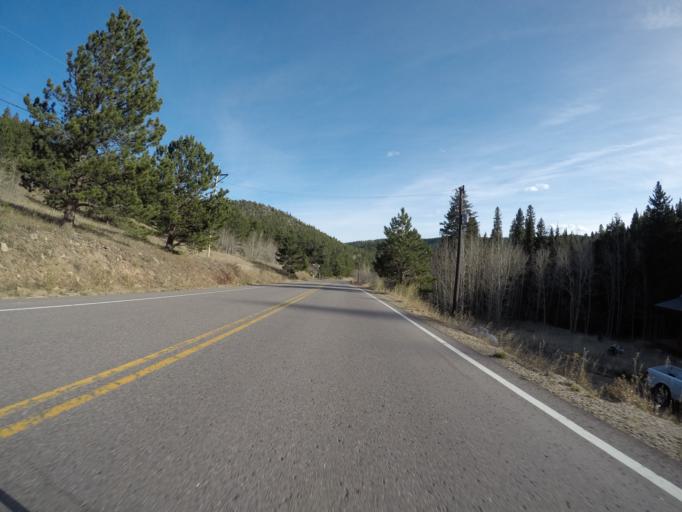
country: US
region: Colorado
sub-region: Boulder County
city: Nederland
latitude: 40.0640
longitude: -105.5005
